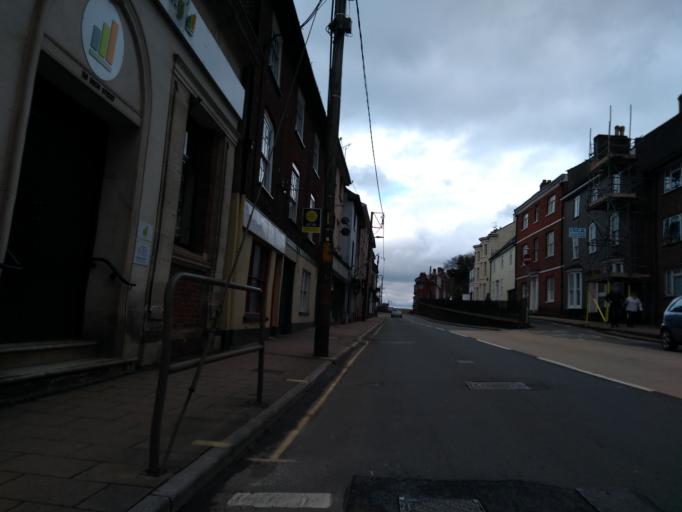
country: GB
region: England
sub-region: Devon
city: Crediton
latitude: 50.7903
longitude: -3.6574
